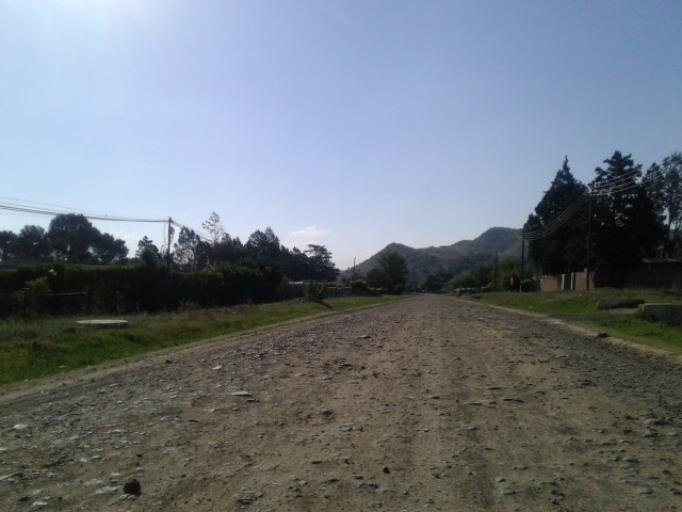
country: LS
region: Maseru
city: Maseru
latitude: -29.3029
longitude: 27.4660
